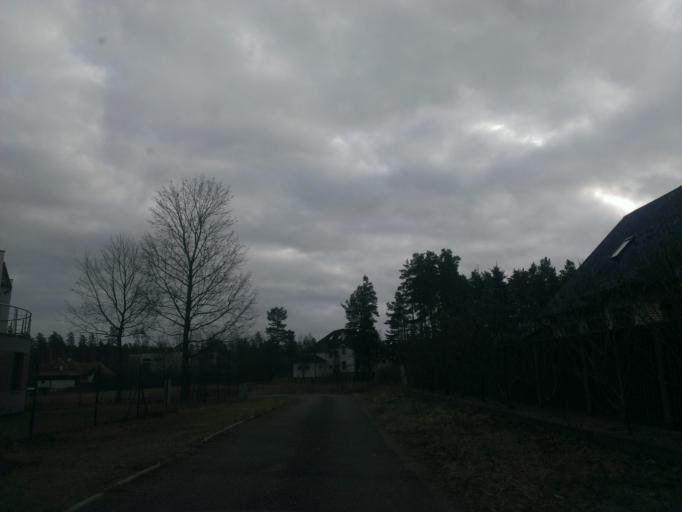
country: LV
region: Riga
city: Bergi
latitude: 56.9898
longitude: 24.3082
